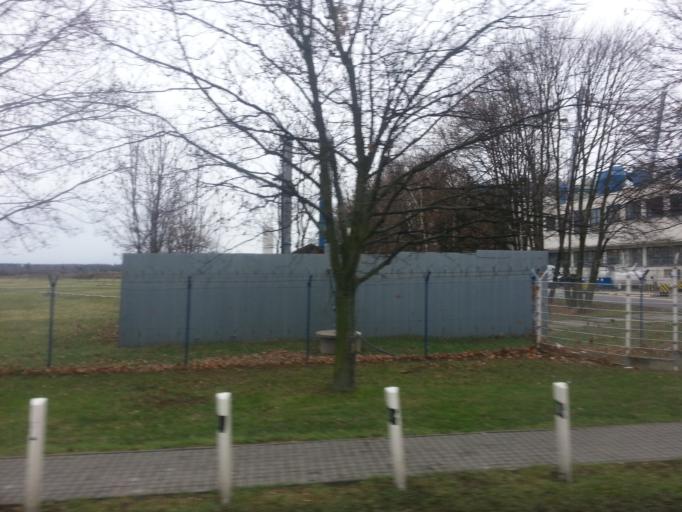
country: CZ
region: Central Bohemia
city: Tuchomerice
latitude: 50.1079
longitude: 14.2777
